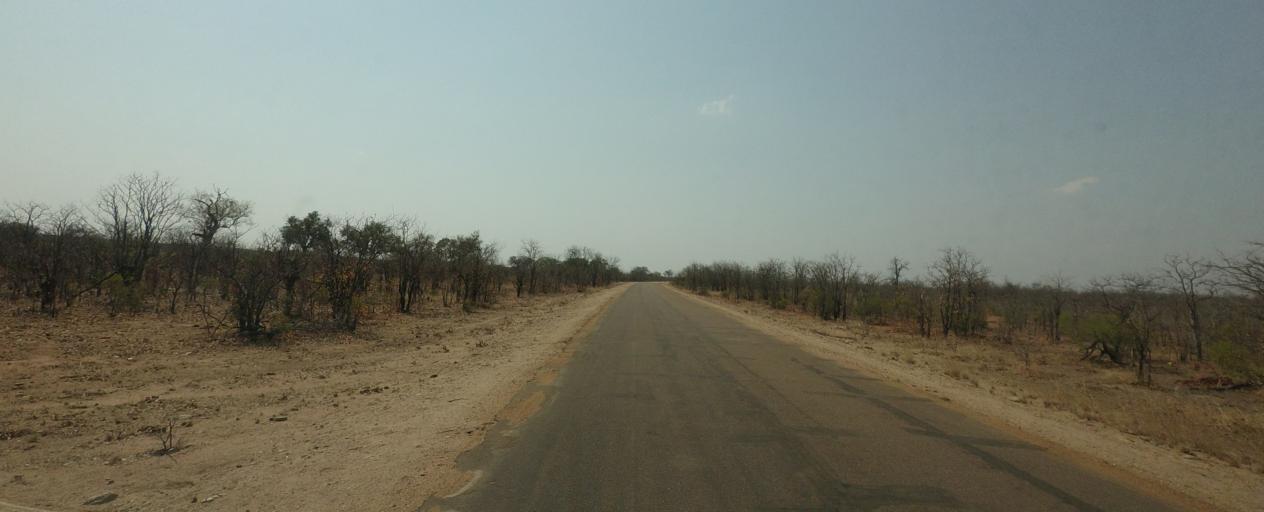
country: ZA
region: Limpopo
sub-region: Mopani District Municipality
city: Phalaborwa
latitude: -23.3718
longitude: 31.3207
